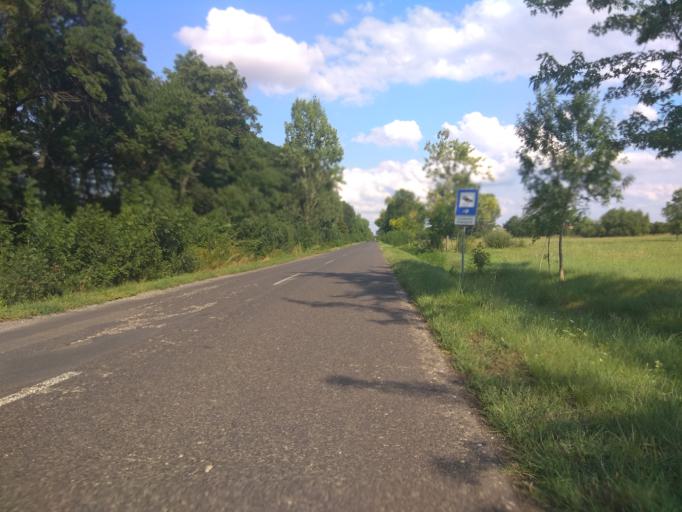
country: HU
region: Borsod-Abauj-Zemplen
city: Mezokeresztes
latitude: 47.8123
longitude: 20.7263
